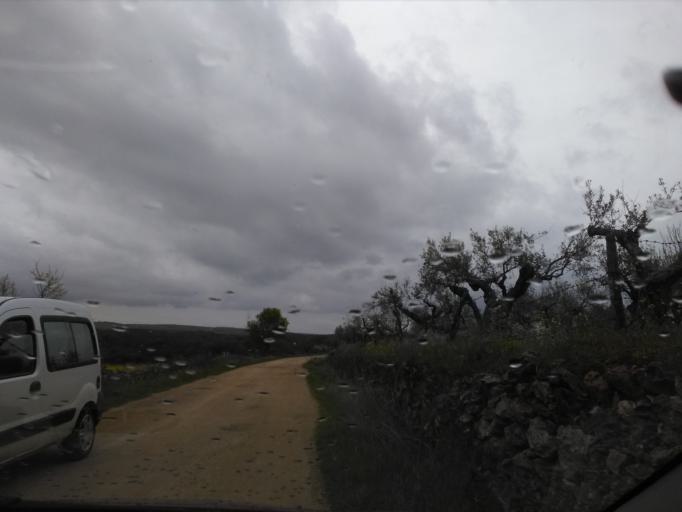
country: ES
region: Castille and Leon
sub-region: Provincia de Salamanca
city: San Felices de los Gallegos
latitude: 40.8404
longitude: -6.7274
